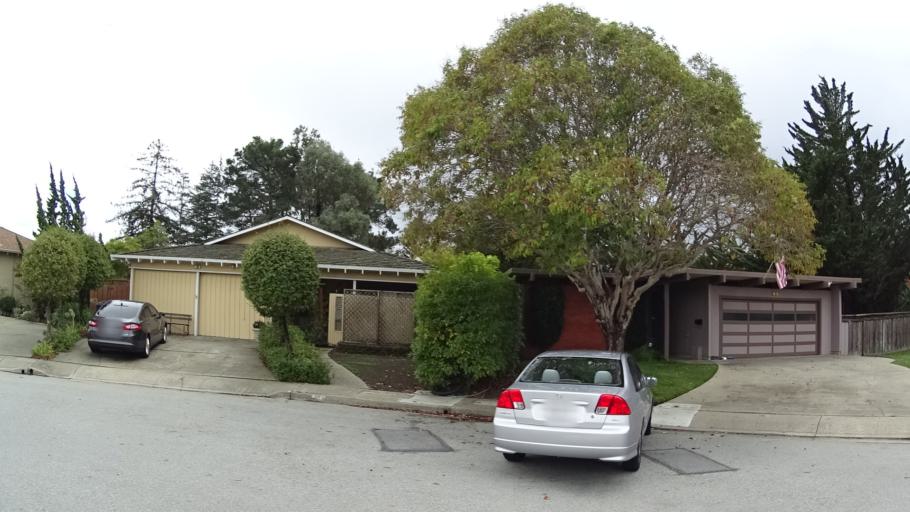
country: US
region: California
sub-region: San Mateo County
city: San Bruno
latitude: 37.6025
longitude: -122.4160
